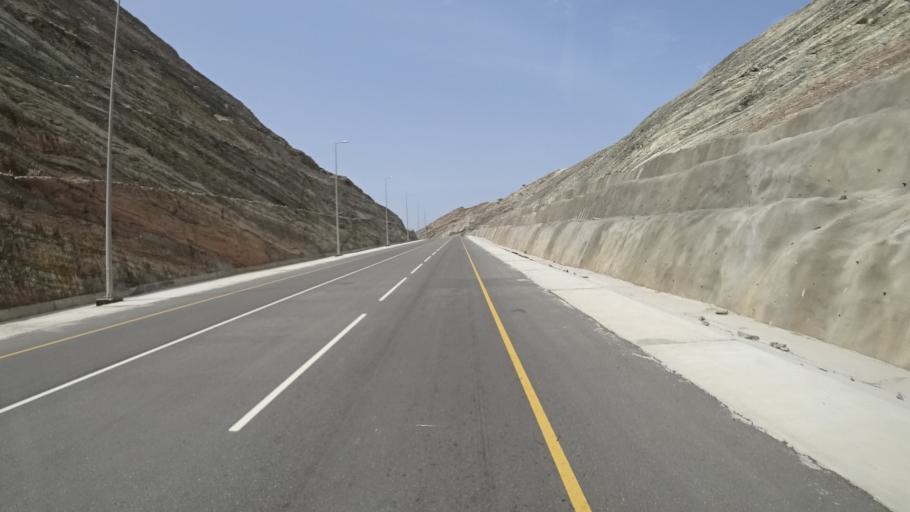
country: OM
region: Muhafazat Masqat
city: Muscat
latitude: 23.4417
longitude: 58.7583
